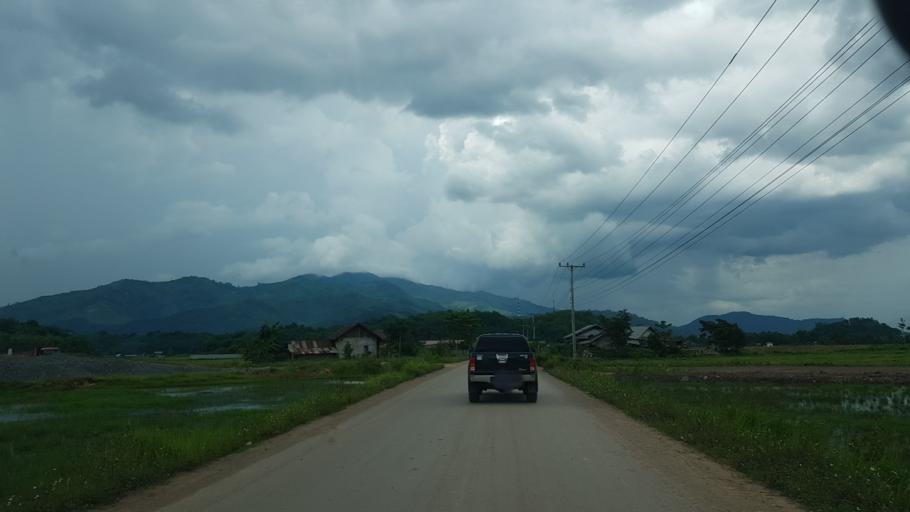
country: LA
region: Oudomxai
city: Muang Xay
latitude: 20.6771
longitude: 101.9702
